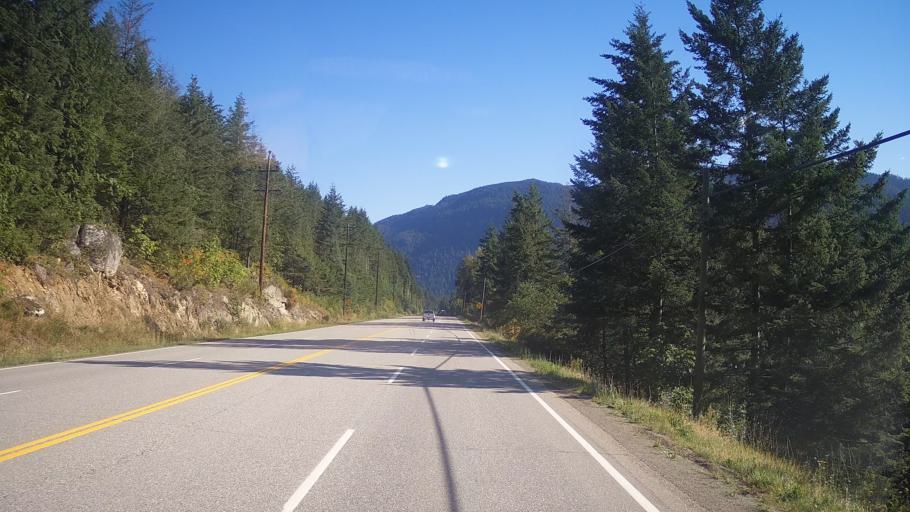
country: CA
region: British Columbia
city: Hope
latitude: 49.6780
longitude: -121.4181
